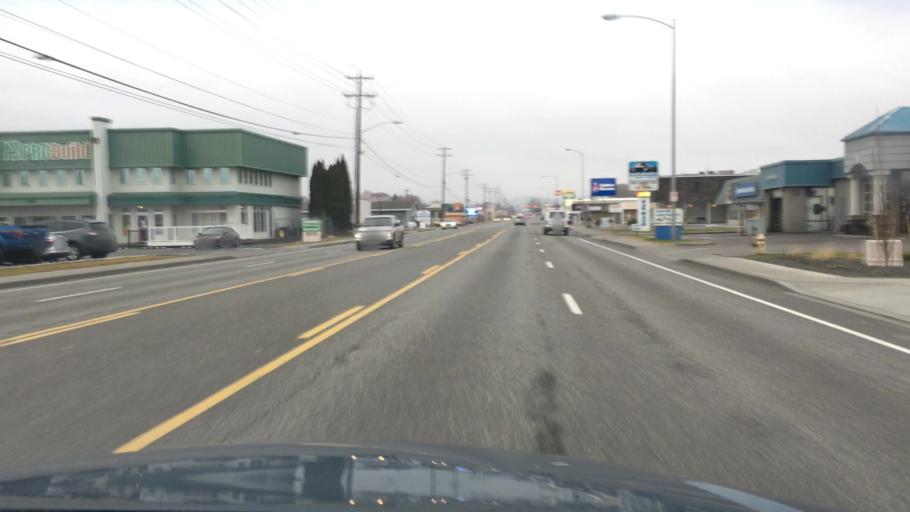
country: US
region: Washington
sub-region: Franklin County
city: West Pasco
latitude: 46.2124
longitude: -119.1730
